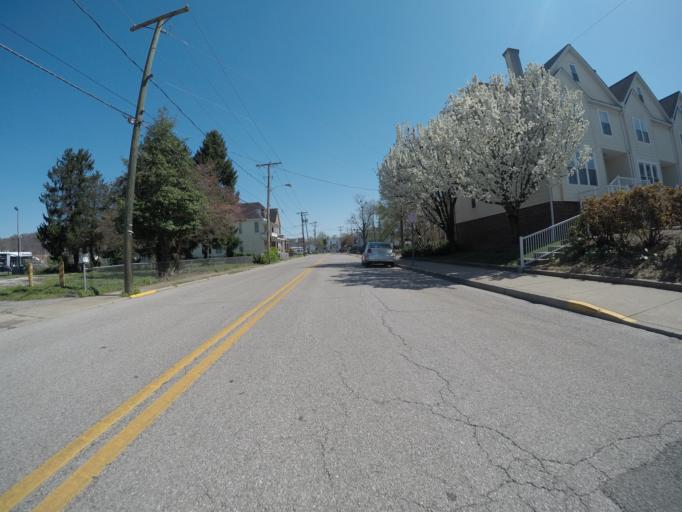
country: US
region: West Virginia
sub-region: Kanawha County
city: Charleston
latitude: 38.3455
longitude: -81.6267
